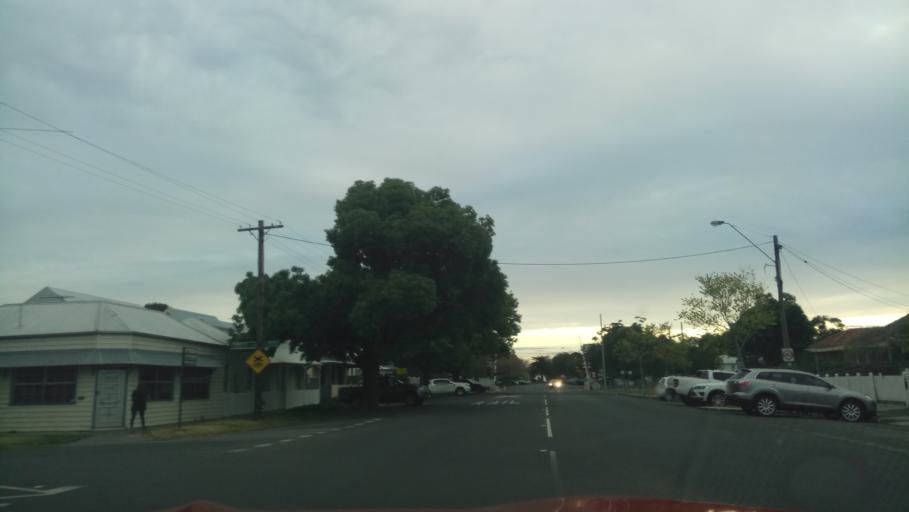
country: AU
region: Victoria
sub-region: Hobsons Bay
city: Williamstown
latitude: -37.8648
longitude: 144.8995
